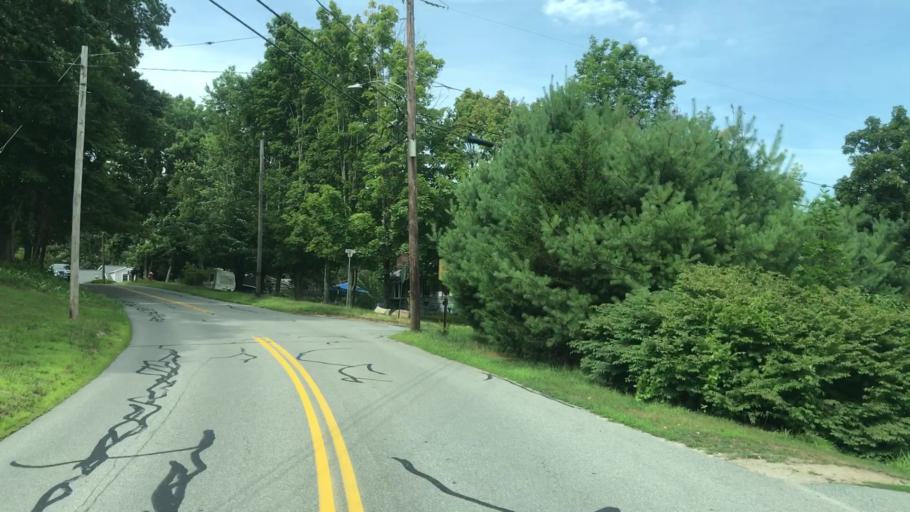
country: US
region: Connecticut
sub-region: New London County
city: Niantic
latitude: 41.3426
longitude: -72.2163
